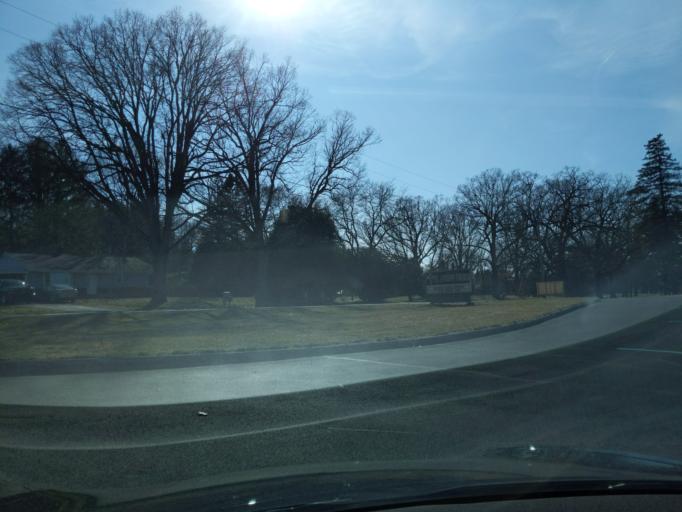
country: US
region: Michigan
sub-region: Ionia County
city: Saranac
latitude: 42.9301
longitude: -85.1948
